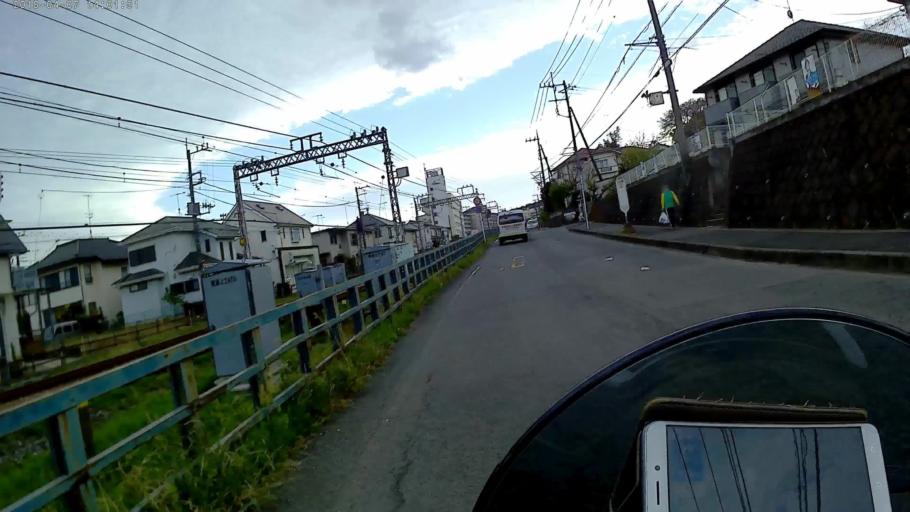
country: JP
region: Kanagawa
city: Hadano
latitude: 35.3700
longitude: 139.2657
